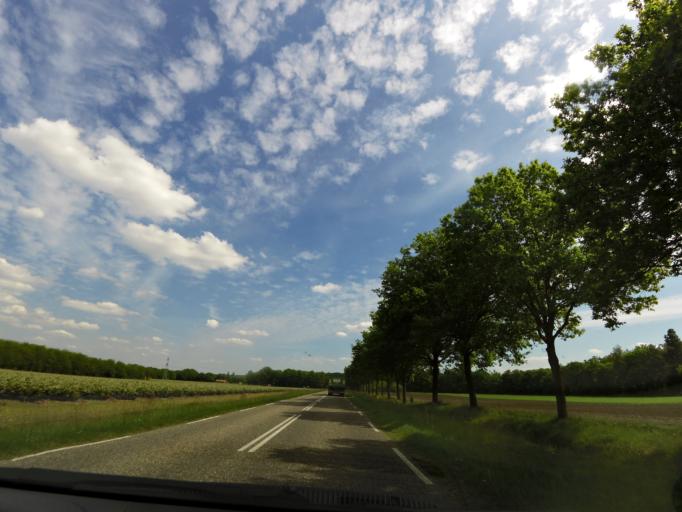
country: NL
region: Limburg
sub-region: Gemeente Leudal
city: Haelen
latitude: 51.2911
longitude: 5.9677
